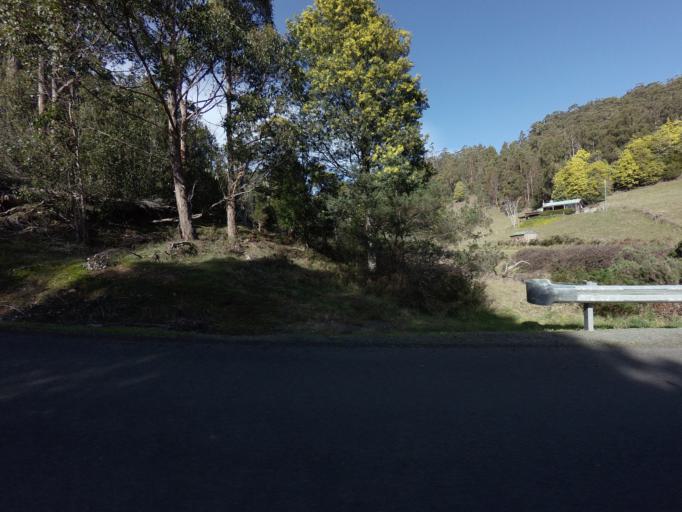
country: AU
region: Tasmania
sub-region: Huon Valley
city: Cygnet
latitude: -43.1746
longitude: 147.1571
